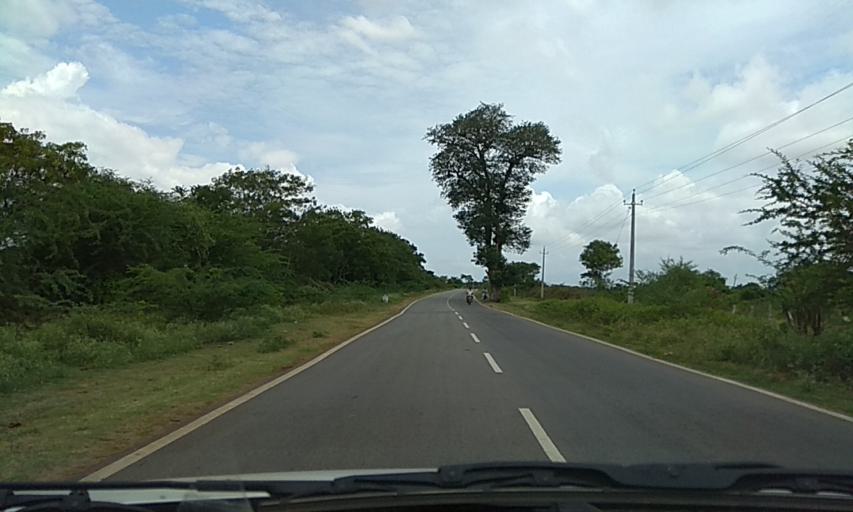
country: IN
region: Karnataka
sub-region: Chamrajnagar
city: Gundlupet
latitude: 11.8121
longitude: 76.7463
